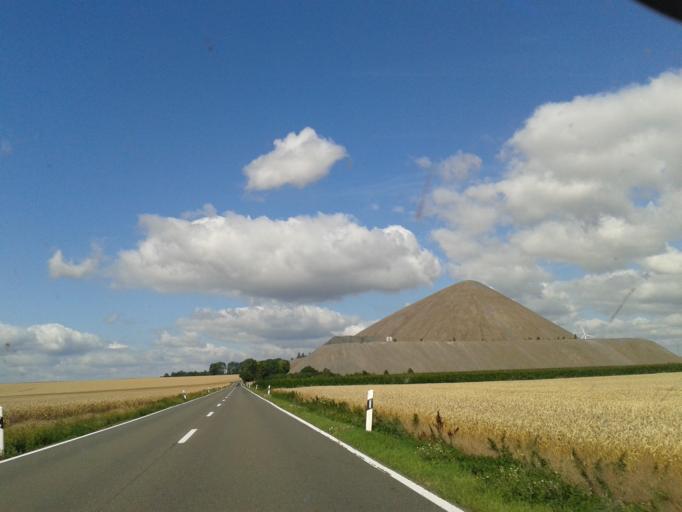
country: DE
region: Saxony-Anhalt
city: Polleben
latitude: 51.5797
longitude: 11.5749
